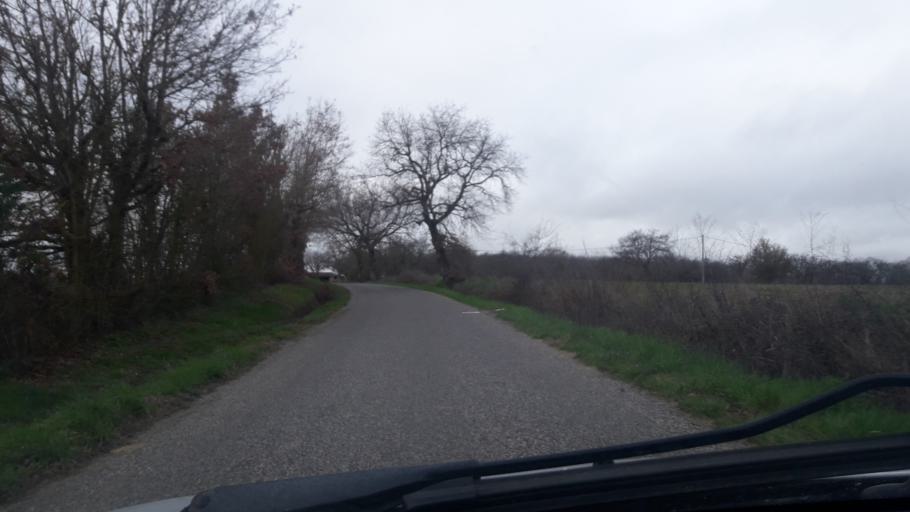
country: FR
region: Midi-Pyrenees
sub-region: Departement du Gers
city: Gimont
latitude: 43.6497
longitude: 0.9901
